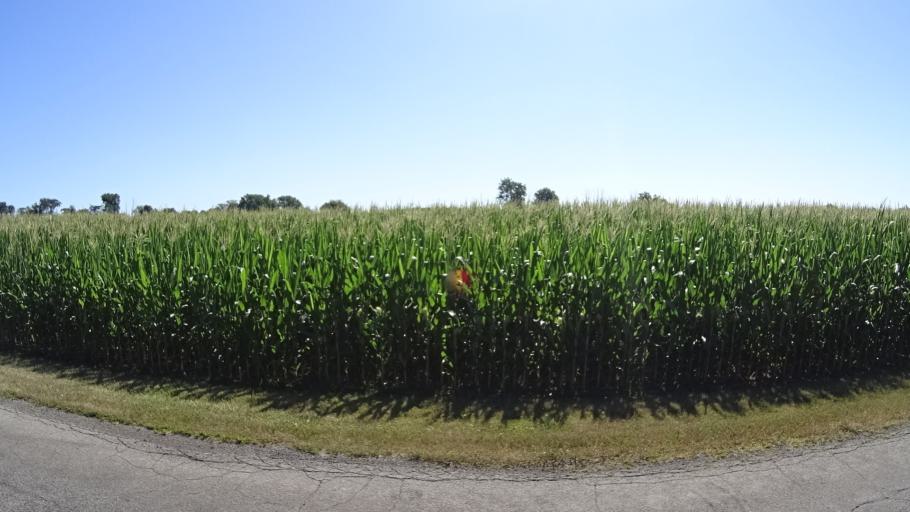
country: US
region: Ohio
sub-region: Erie County
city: Sandusky
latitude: 41.3827
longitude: -82.7102
